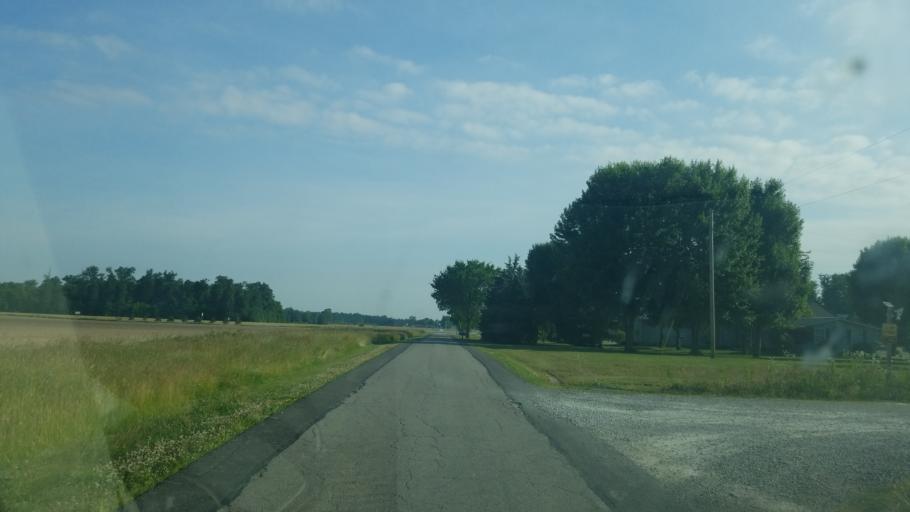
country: US
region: Ohio
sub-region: Hancock County
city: Arlington
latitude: 40.8240
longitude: -83.6705
